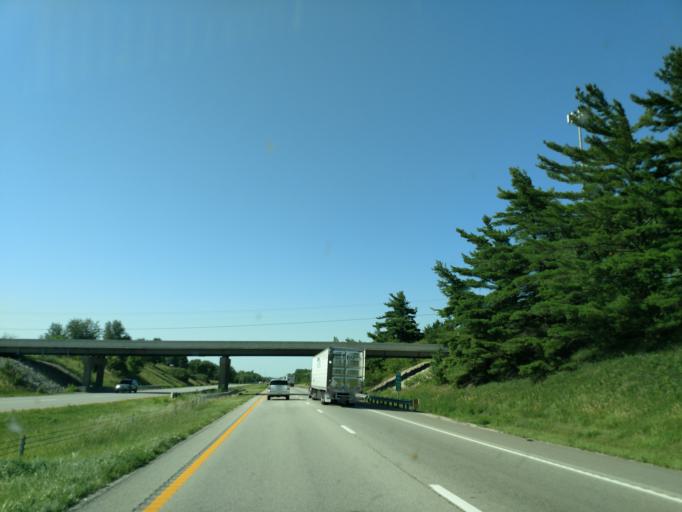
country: US
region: Missouri
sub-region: Buchanan County
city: Saint Joseph
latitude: 39.6817
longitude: -94.7881
